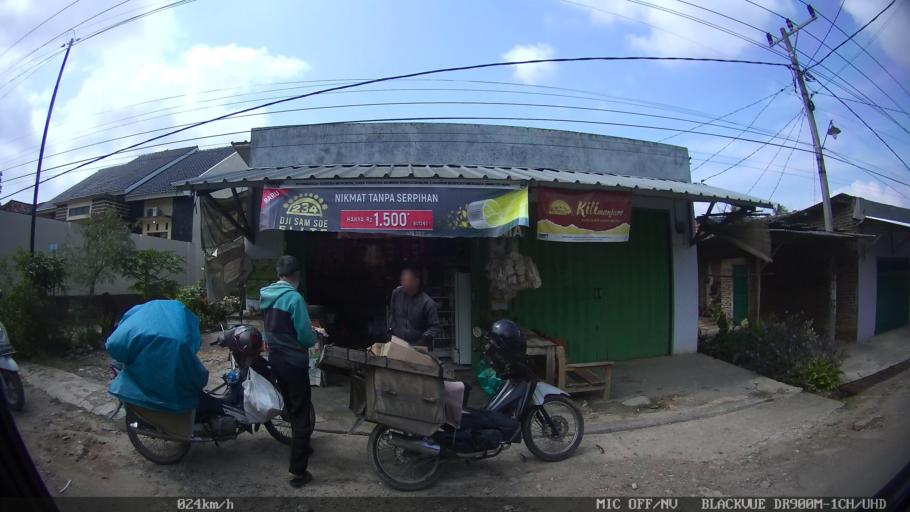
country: ID
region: Lampung
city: Kedaton
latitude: -5.3419
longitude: 105.2896
